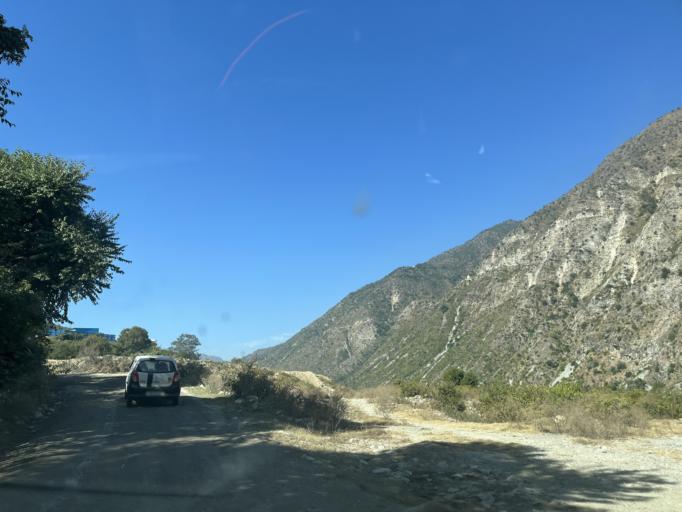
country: IN
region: Uttarakhand
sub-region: Almora
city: Ranikhet
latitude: 29.5507
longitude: 79.4044
